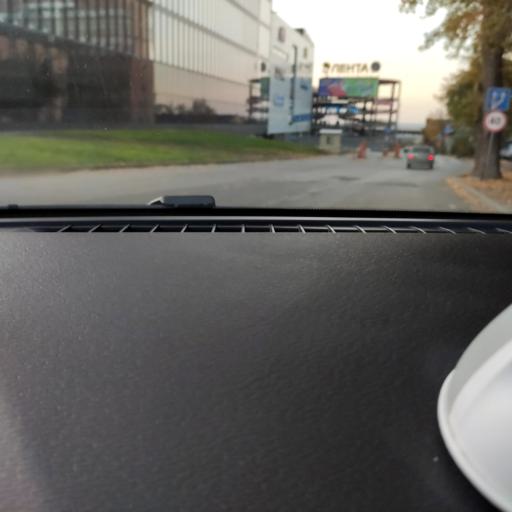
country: RU
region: Samara
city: Samara
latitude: 53.1874
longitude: 50.1247
